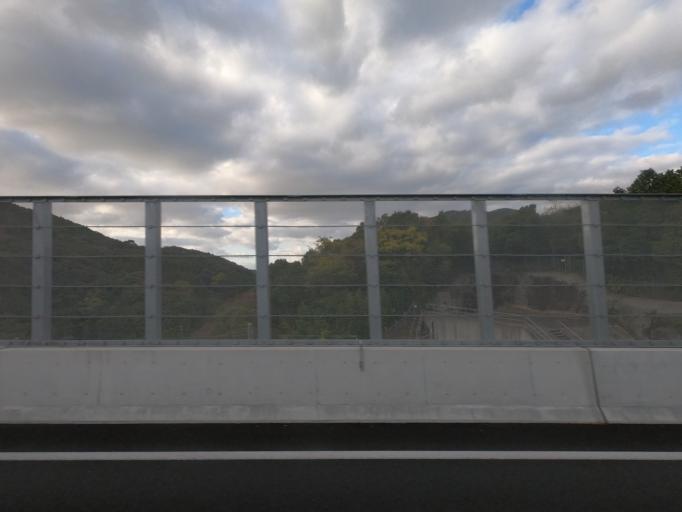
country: JP
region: Kumamoto
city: Minamata
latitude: 32.2305
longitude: 130.4500
